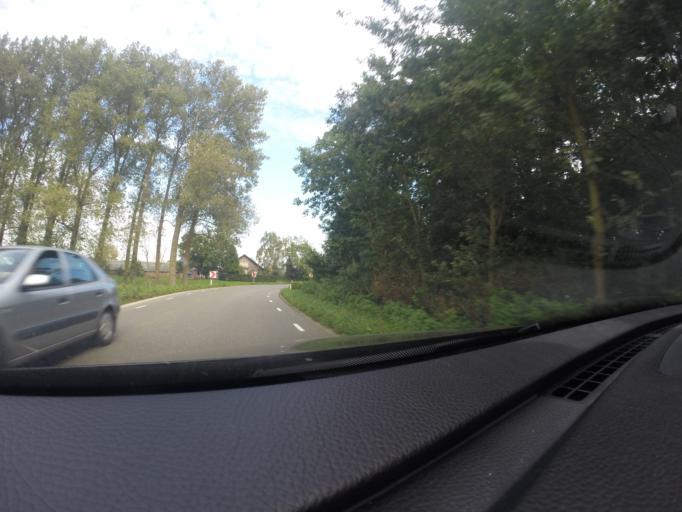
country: NL
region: Gelderland
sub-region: Gemeente Doetinchem
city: Doetinchem
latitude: 52.0067
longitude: 6.2522
